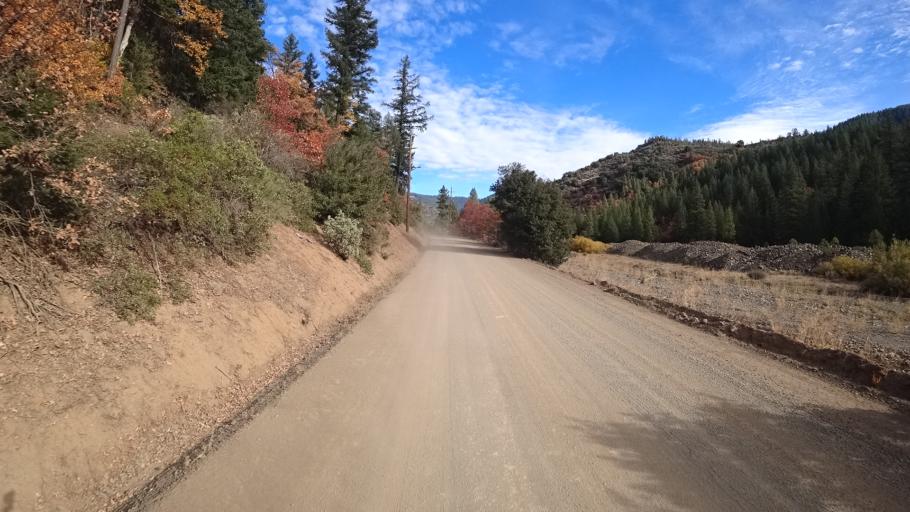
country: US
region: California
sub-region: Siskiyou County
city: Yreka
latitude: 41.6979
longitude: -122.8178
